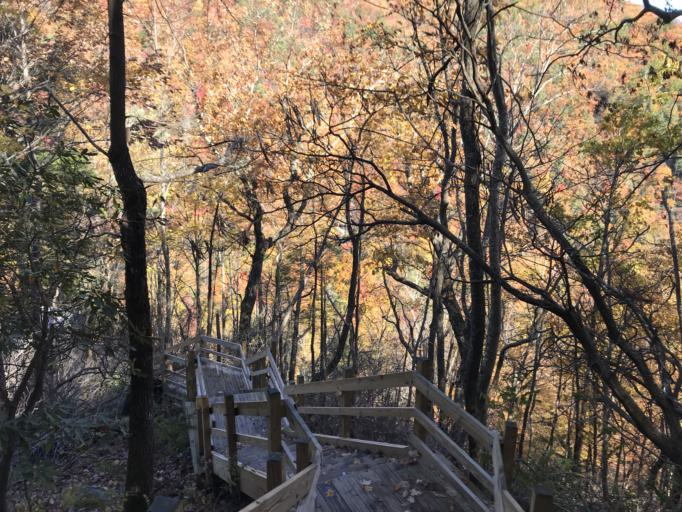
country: US
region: South Carolina
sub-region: Oconee County
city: Walhalla
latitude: 35.0335
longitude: -83.0162
